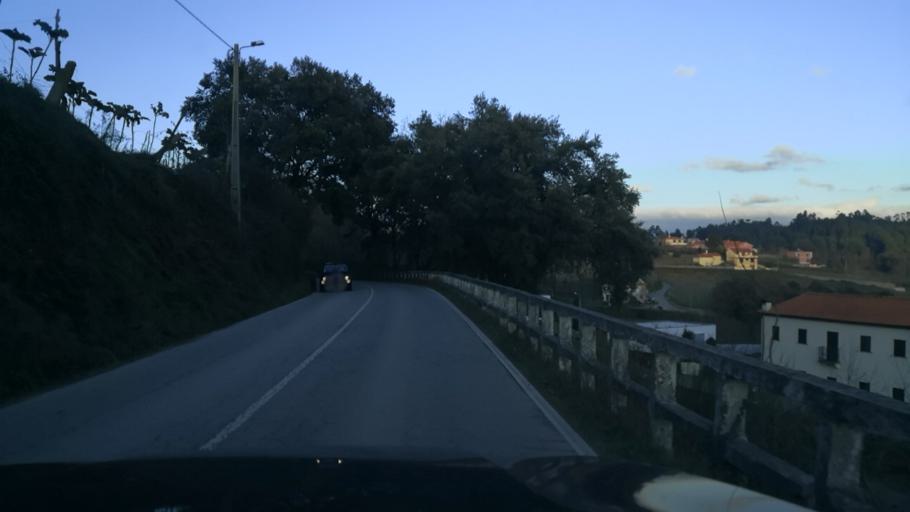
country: PT
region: Vila Real
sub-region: Mondim de Basto
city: Mondim de Basto
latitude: 41.4461
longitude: -7.9643
